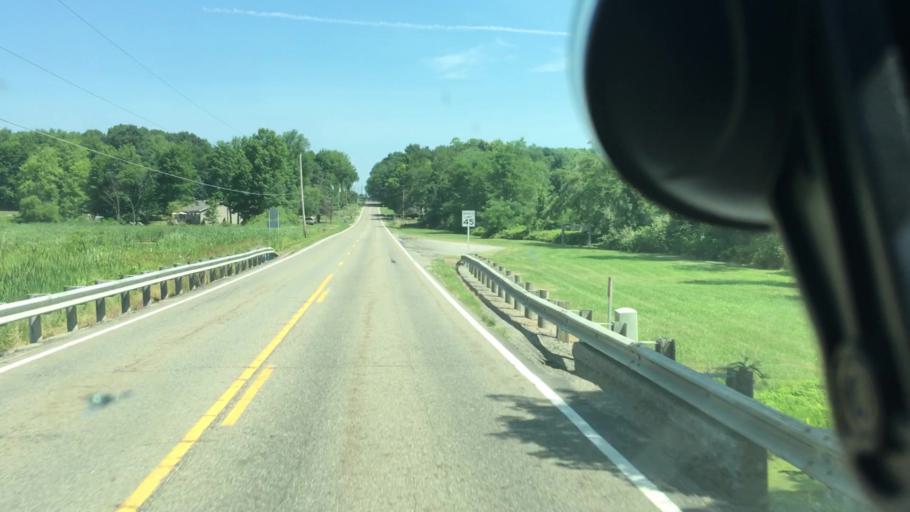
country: US
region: Ohio
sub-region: Columbiana County
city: Lisbon
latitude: 40.7961
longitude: -80.8586
